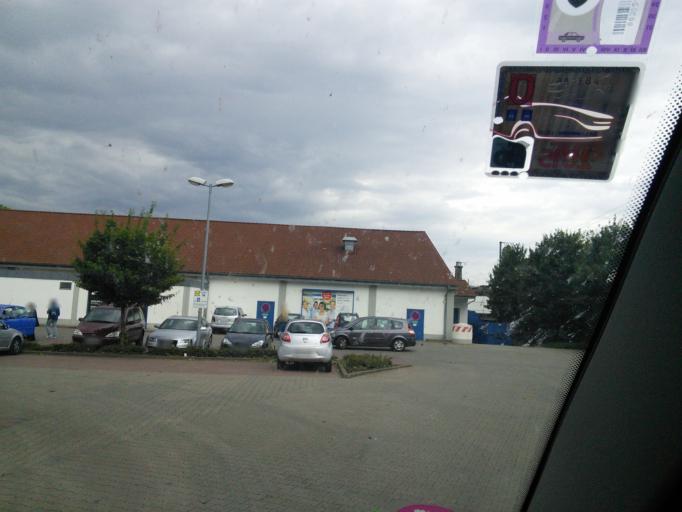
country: DE
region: North Rhine-Westphalia
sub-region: Regierungsbezirk Koln
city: Neuehrenfeld
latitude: 50.9508
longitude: 6.9077
